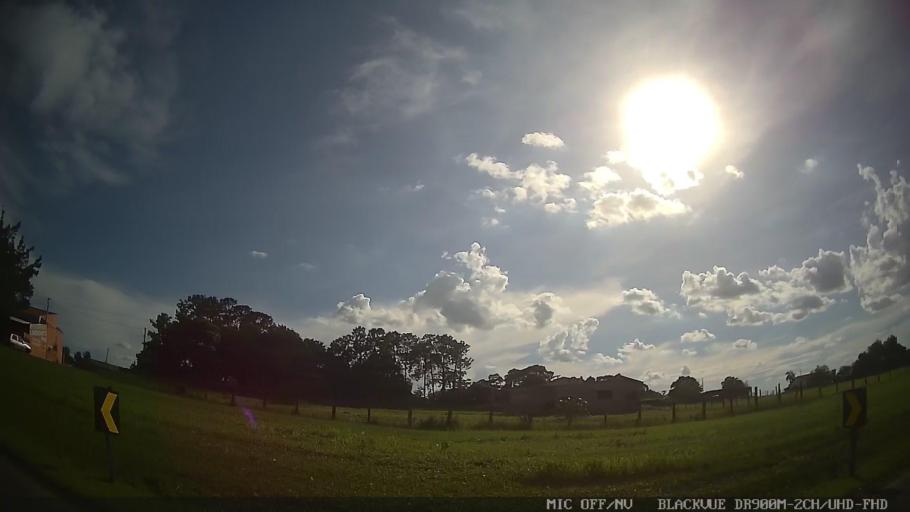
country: BR
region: Sao Paulo
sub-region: Laranjal Paulista
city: Laranjal Paulista
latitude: -23.0776
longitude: -47.8080
